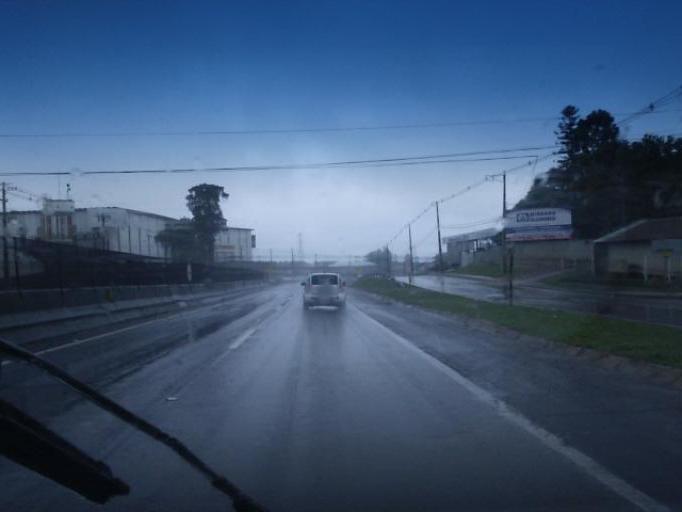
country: BR
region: Parana
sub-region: Sao Jose Dos Pinhais
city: Sao Jose dos Pinhais
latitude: -25.5850
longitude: -49.1751
